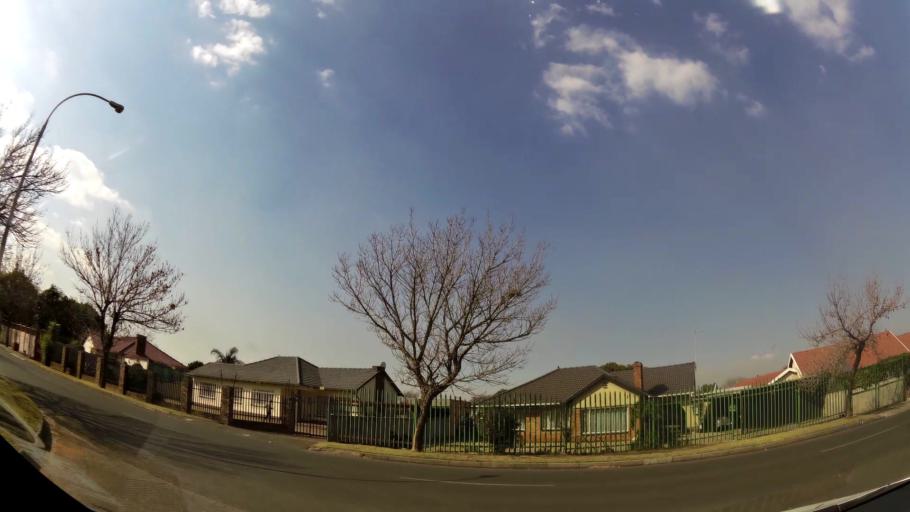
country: ZA
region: Gauteng
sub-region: Ekurhuleni Metropolitan Municipality
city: Germiston
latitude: -26.1831
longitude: 28.1945
